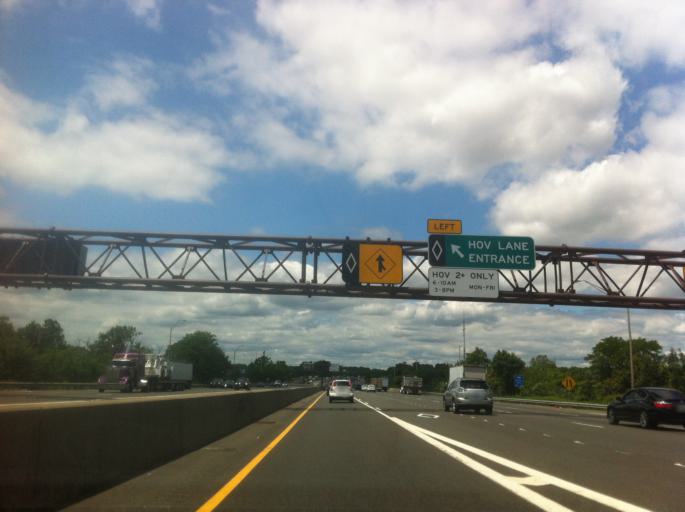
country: US
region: New York
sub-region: Nassau County
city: Old Bethpage
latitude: 40.7847
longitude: -73.4417
